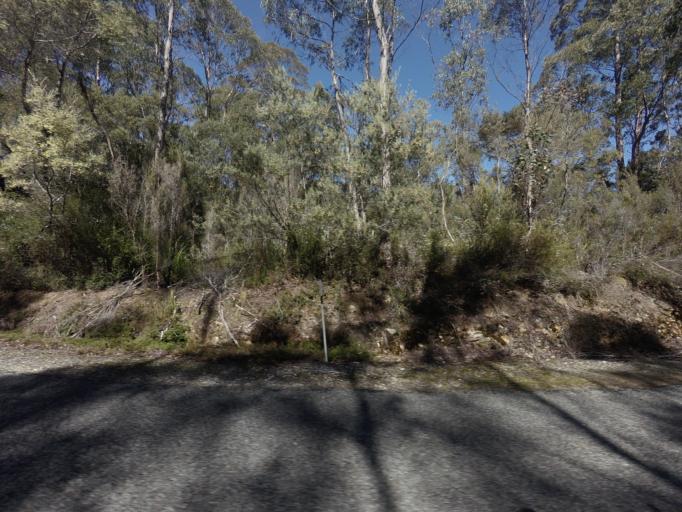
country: AU
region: Tasmania
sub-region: Derwent Valley
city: New Norfolk
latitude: -42.7410
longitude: 146.4190
